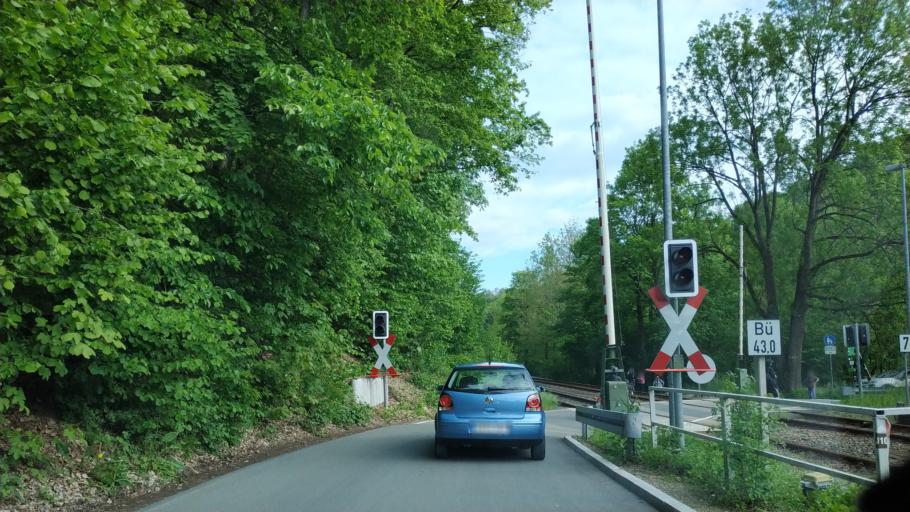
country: DE
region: Saxony
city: Pohl
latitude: 50.5576
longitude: 12.1641
